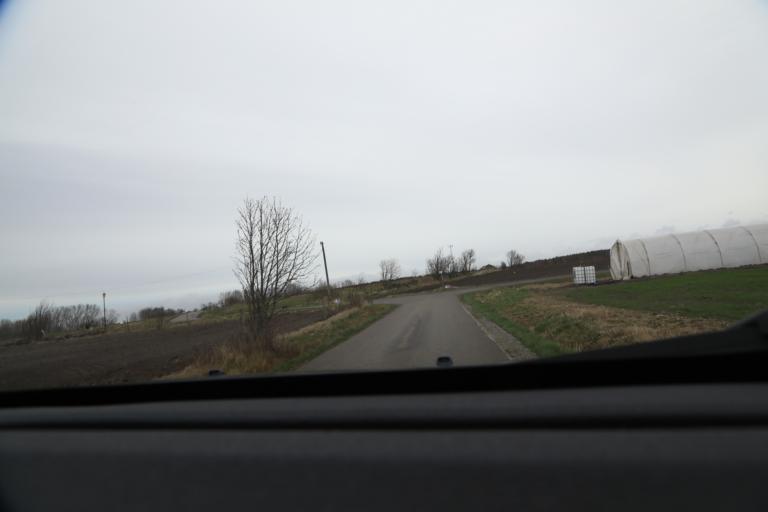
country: SE
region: Halland
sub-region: Varbergs Kommun
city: Traslovslage
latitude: 57.0763
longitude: 12.3037
